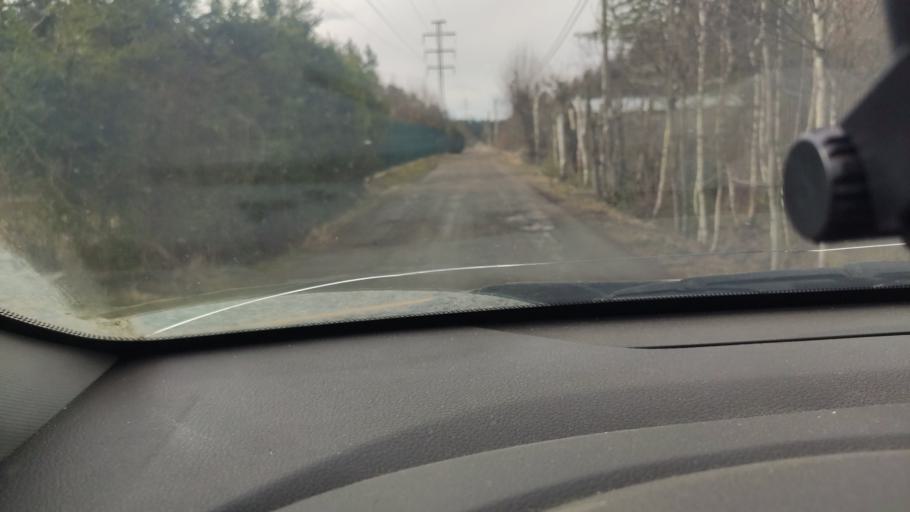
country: RU
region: Moskovskaya
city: Chupryakovo
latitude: 55.5830
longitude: 36.6024
